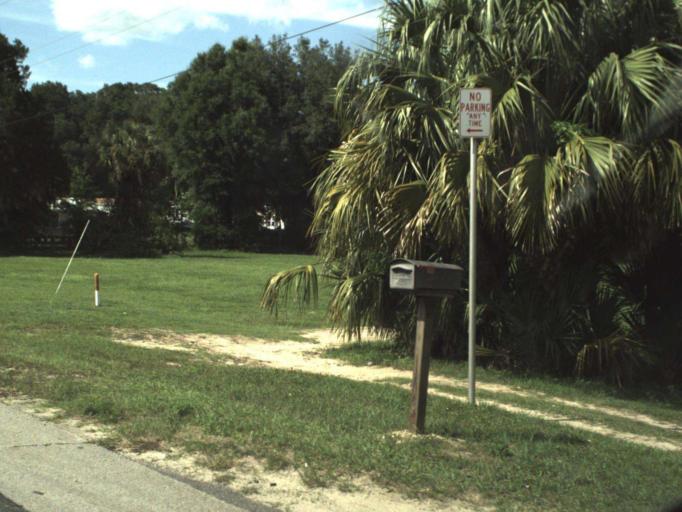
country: US
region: Florida
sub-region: Marion County
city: Ocala
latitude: 29.1253
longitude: -82.1021
